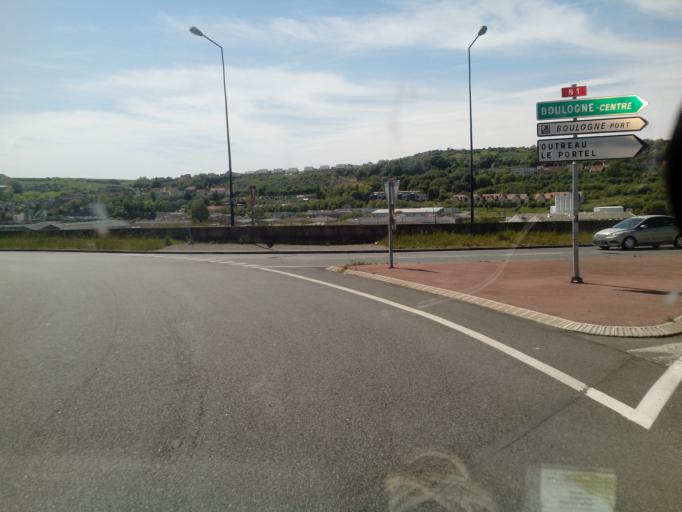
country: FR
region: Nord-Pas-de-Calais
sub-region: Departement du Pas-de-Calais
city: Saint-Leonard
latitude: 50.6972
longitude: 1.6119
